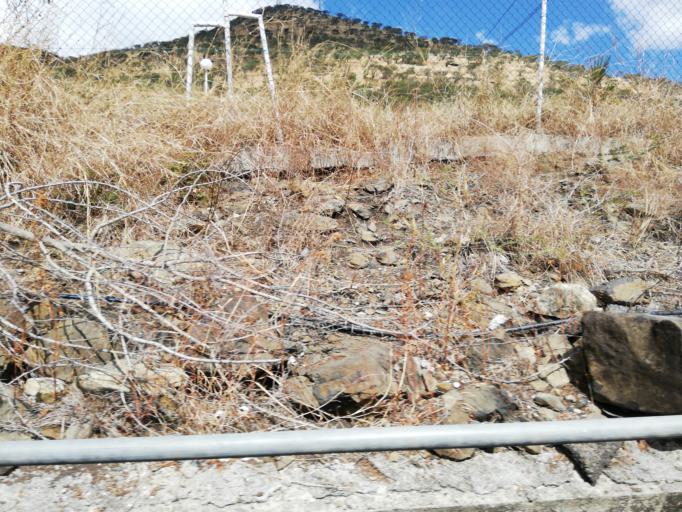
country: MU
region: Port Louis
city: Port Louis
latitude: -20.1768
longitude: 57.5079
